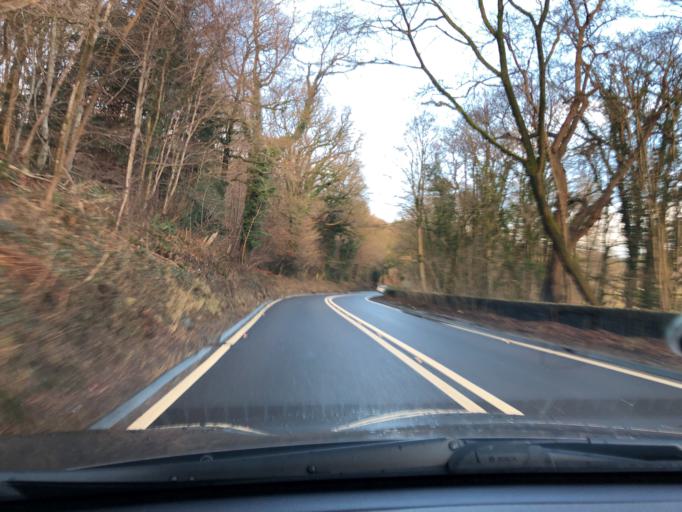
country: GB
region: England
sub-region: Cumbria
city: Ulverston
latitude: 54.2420
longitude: -3.0482
